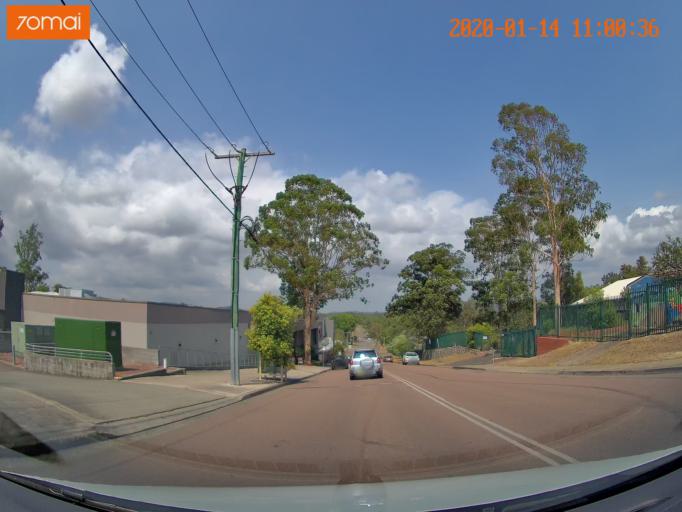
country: AU
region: New South Wales
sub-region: Lake Macquarie Shire
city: Dora Creek
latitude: -33.1059
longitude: 151.4885
